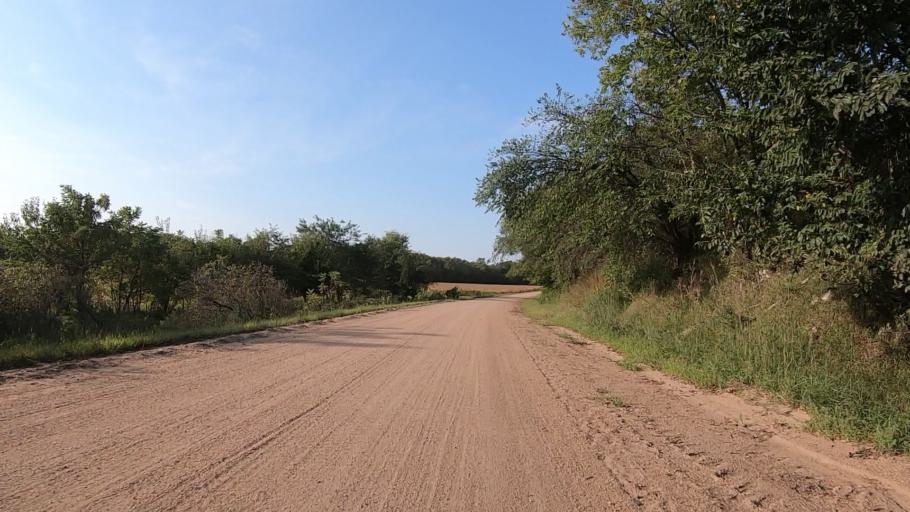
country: US
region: Kansas
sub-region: Marshall County
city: Blue Rapids
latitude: 39.6646
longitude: -96.8155
